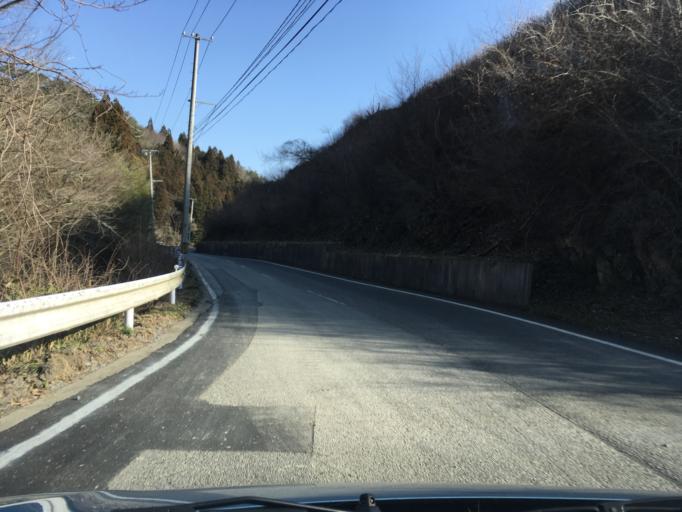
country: JP
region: Iwate
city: Ichinoseki
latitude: 38.7899
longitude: 141.4511
